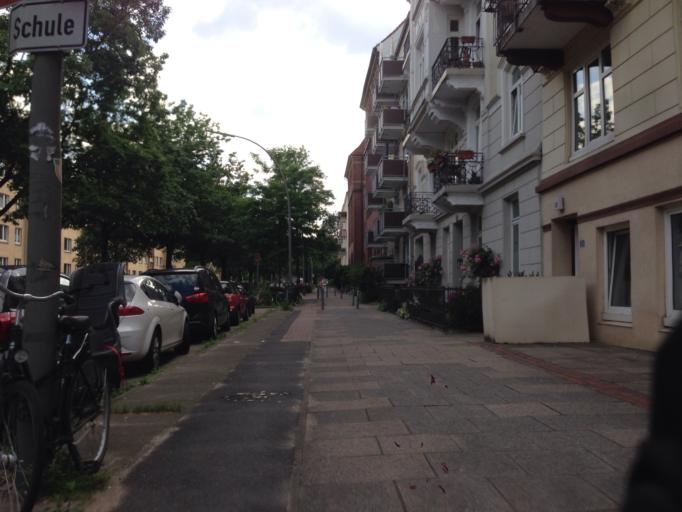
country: DE
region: Hamburg
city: Hamburg-Nord
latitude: 53.5922
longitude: 9.9863
